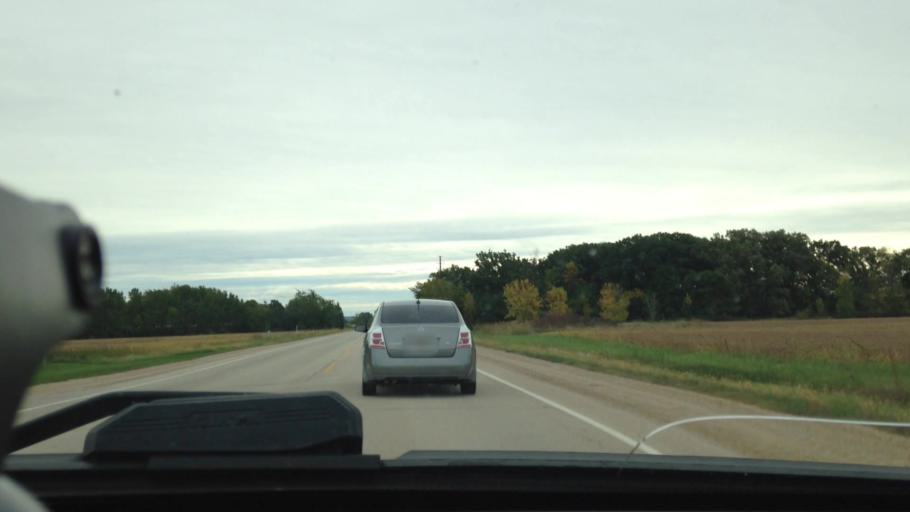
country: US
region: Wisconsin
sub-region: Fond du Lac County
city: North Fond du Lac
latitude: 43.8018
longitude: -88.4969
